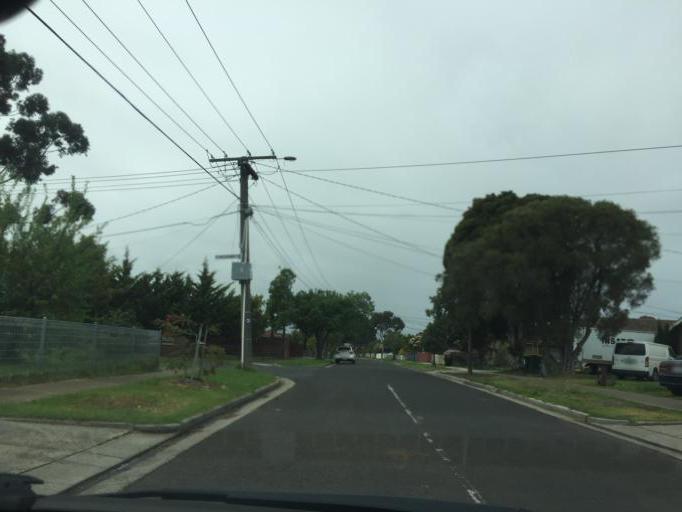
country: AU
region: Victoria
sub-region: Brimbank
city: Sunshine West
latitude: -37.8036
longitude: 144.8226
